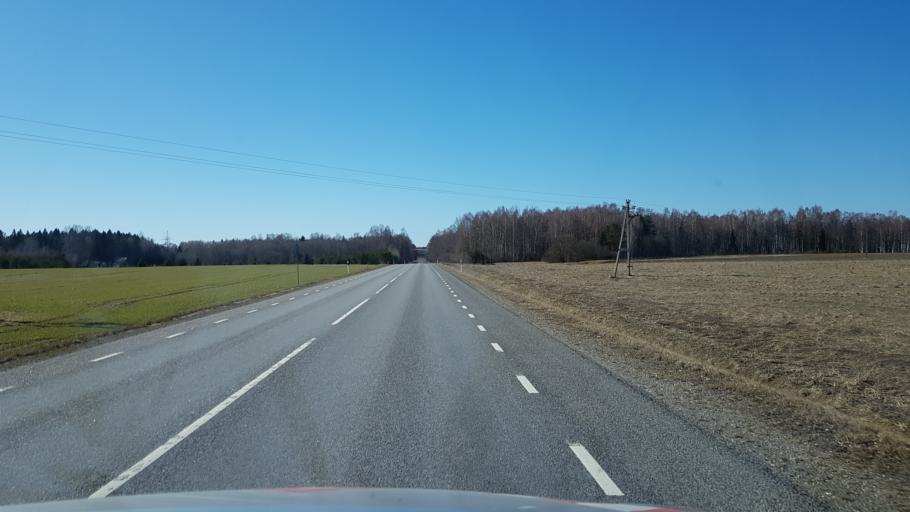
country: EE
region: Laeaene-Virumaa
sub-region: Viru-Nigula vald
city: Kunda
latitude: 59.3618
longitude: 26.6217
